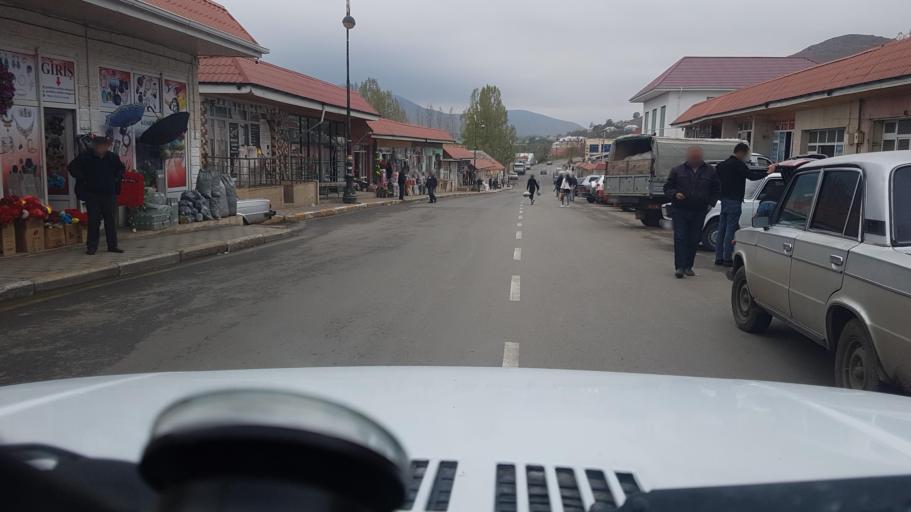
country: AZ
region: Gadabay Rayon
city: Kyadabek
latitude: 40.5737
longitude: 45.8067
